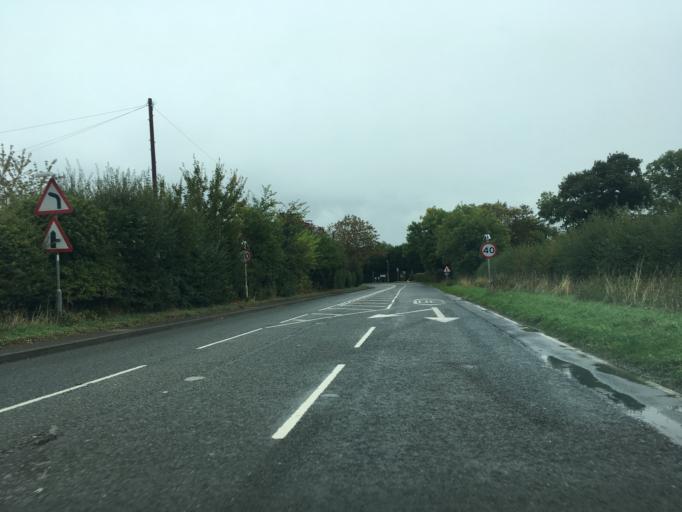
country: GB
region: England
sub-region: Nottinghamshire
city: Ruddington
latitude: 52.8654
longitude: -1.1314
